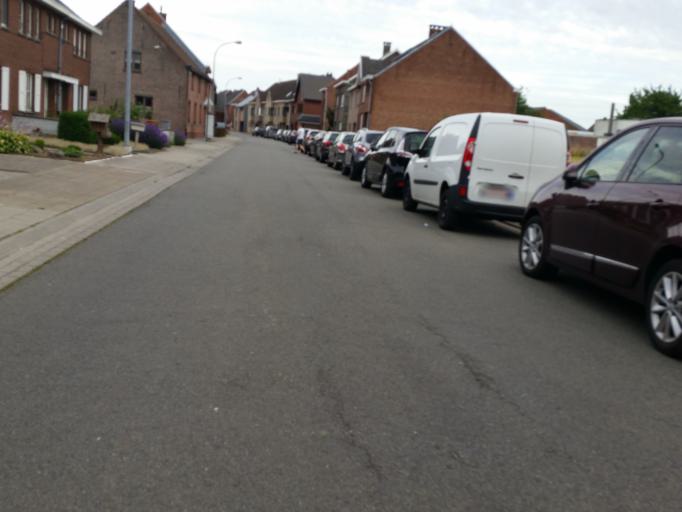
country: BE
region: Flanders
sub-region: Provincie Vlaams-Brabant
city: Kapelle-op-den-Bos
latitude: 51.0318
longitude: 4.3617
